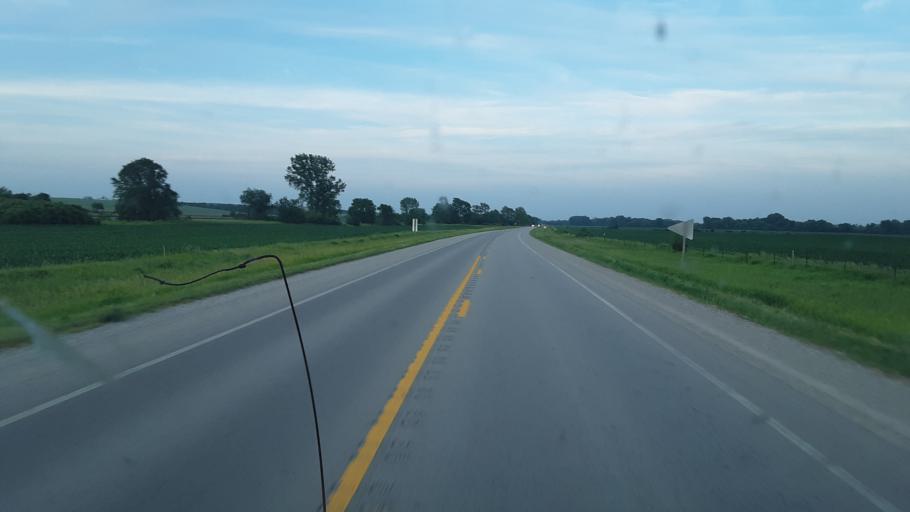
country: US
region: Iowa
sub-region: Benton County
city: Belle Plaine
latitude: 41.7424
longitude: -92.2392
